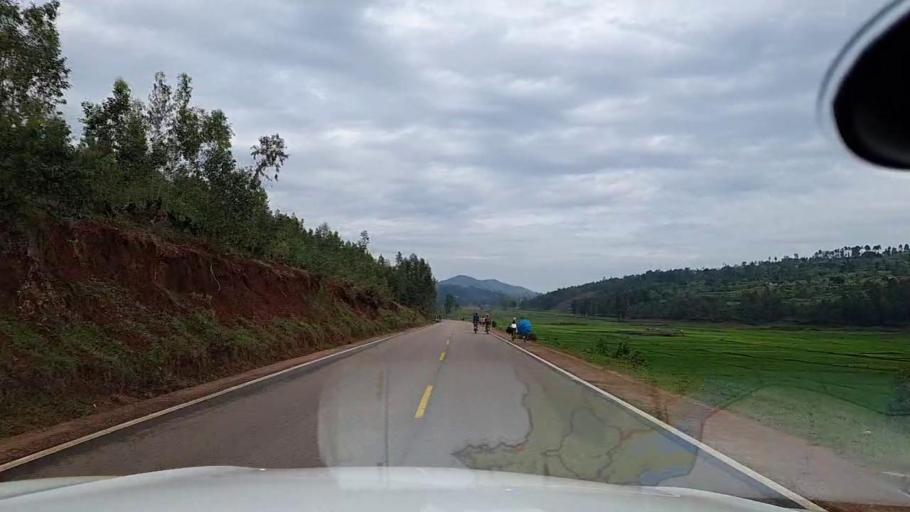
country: RW
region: Southern Province
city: Butare
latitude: -2.5686
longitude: 29.7291
